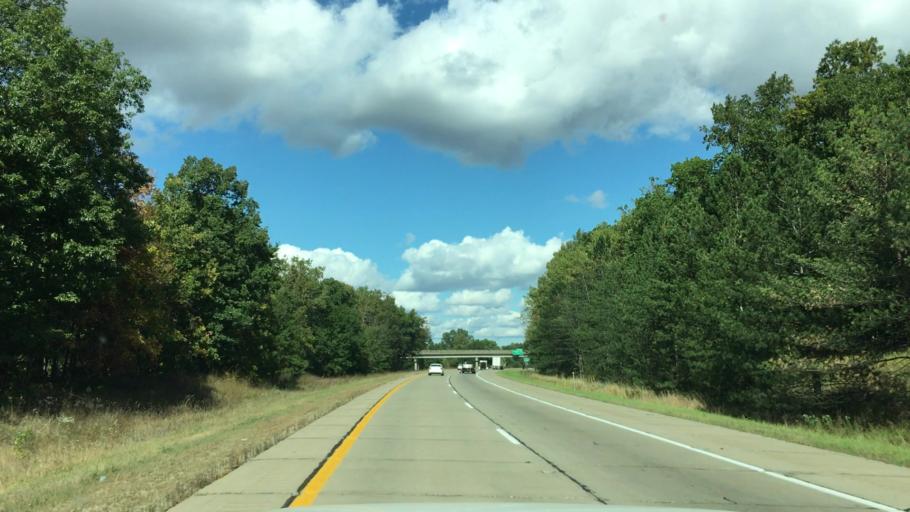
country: US
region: Michigan
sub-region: Eaton County
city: Olivet
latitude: 42.4473
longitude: -84.9491
